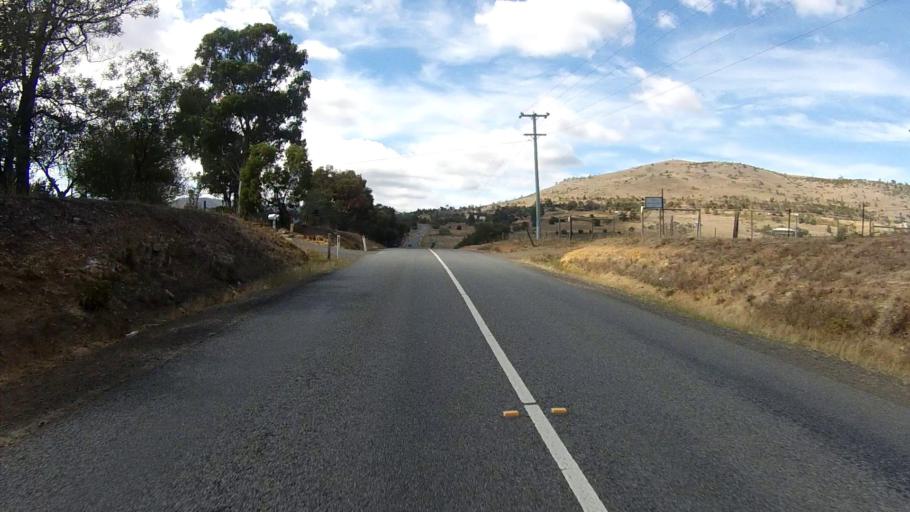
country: AU
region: Tasmania
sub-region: Glenorchy
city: Austins Ferry
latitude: -42.7213
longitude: 147.2802
